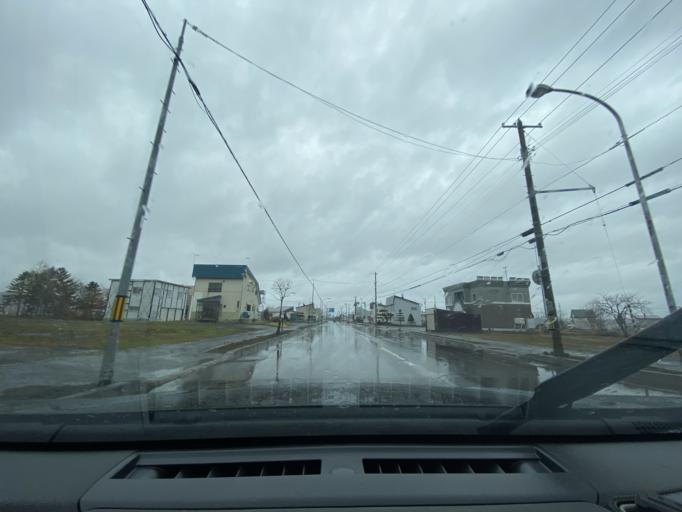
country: JP
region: Hokkaido
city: Fukagawa
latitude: 43.8089
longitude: 142.0256
